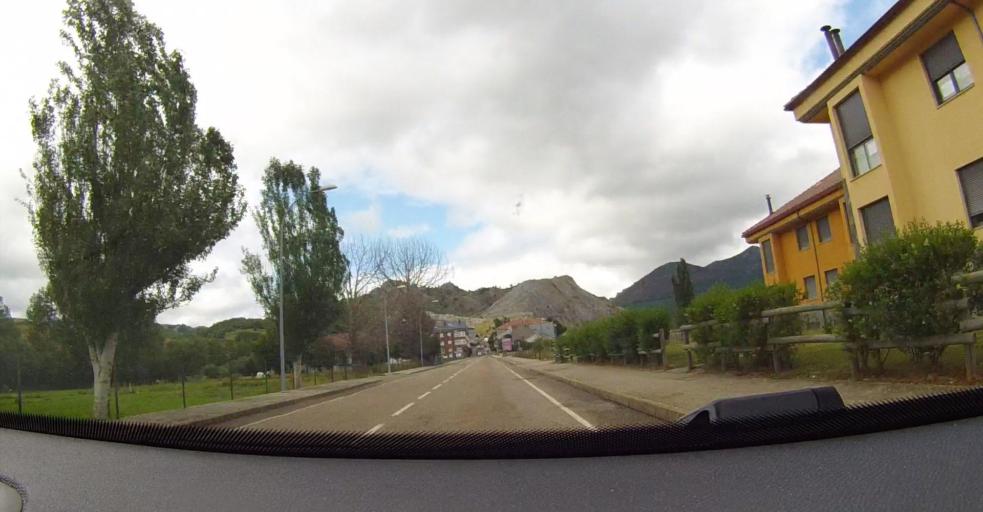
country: ES
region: Castille and Leon
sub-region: Provincia de Leon
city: Puebla de Lillo
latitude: 43.0049
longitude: -5.2701
